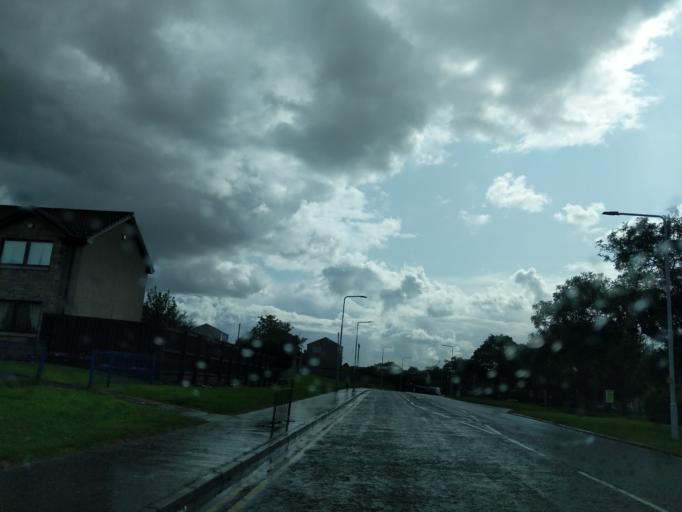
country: GB
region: Scotland
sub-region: Fife
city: Rosyth
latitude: 56.0308
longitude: -3.4274
